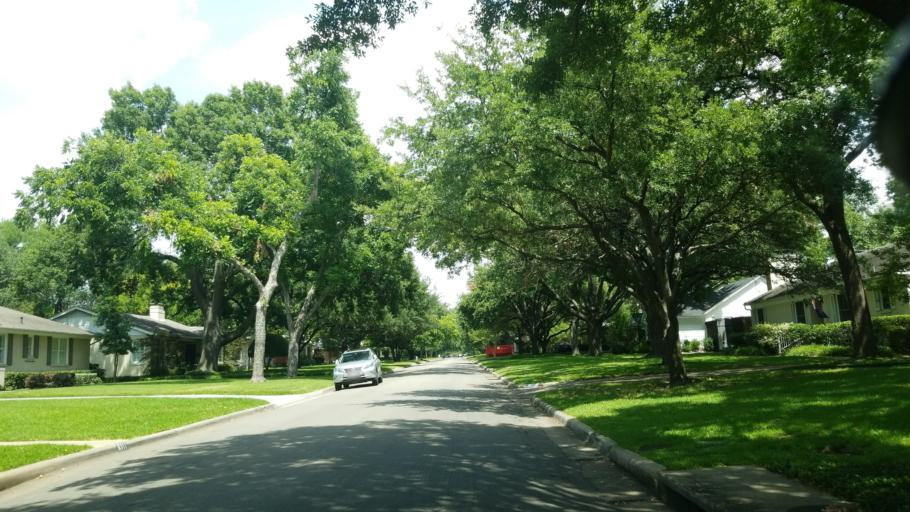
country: US
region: Texas
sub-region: Dallas County
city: University Park
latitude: 32.8684
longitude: -96.8015
